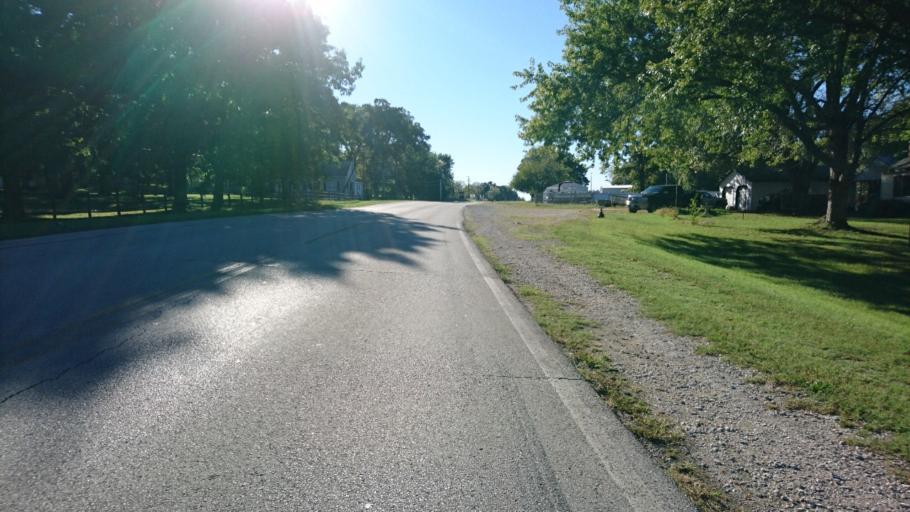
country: US
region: Missouri
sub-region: Jasper County
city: Carthage
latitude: 37.1732
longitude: -94.3503
